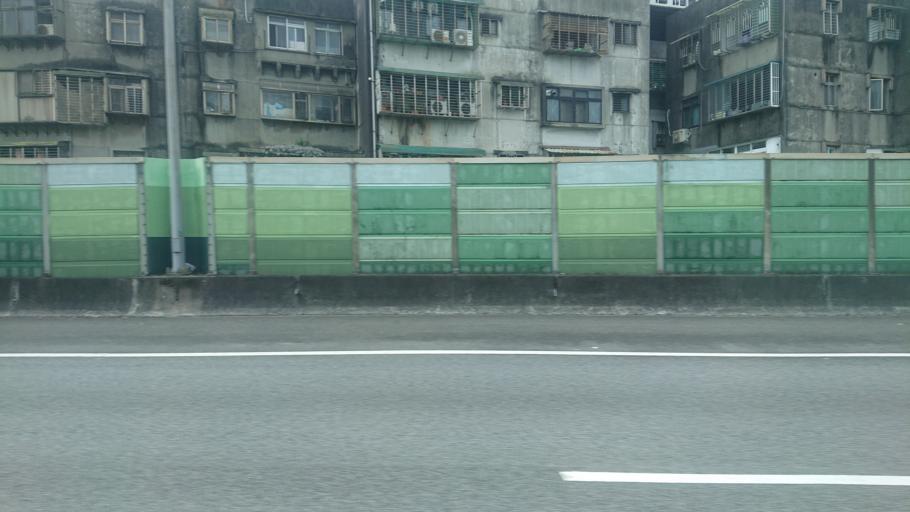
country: TW
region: Taipei
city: Taipei
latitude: 25.0678
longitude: 121.6339
